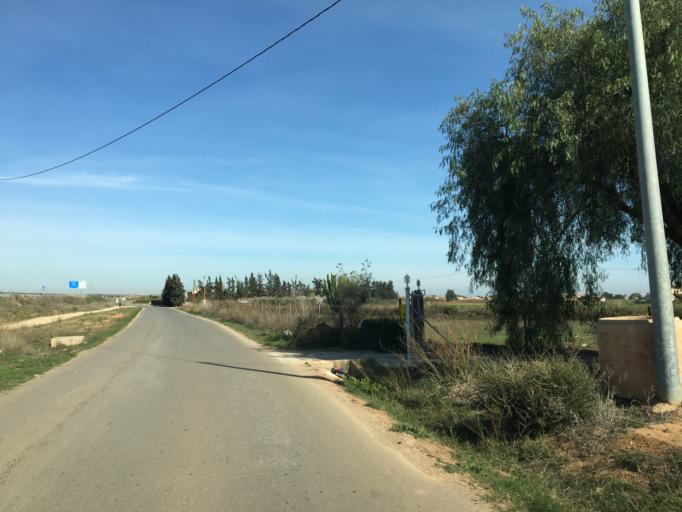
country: ES
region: Murcia
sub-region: Murcia
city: Cartagena
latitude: 37.6553
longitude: -1.0238
